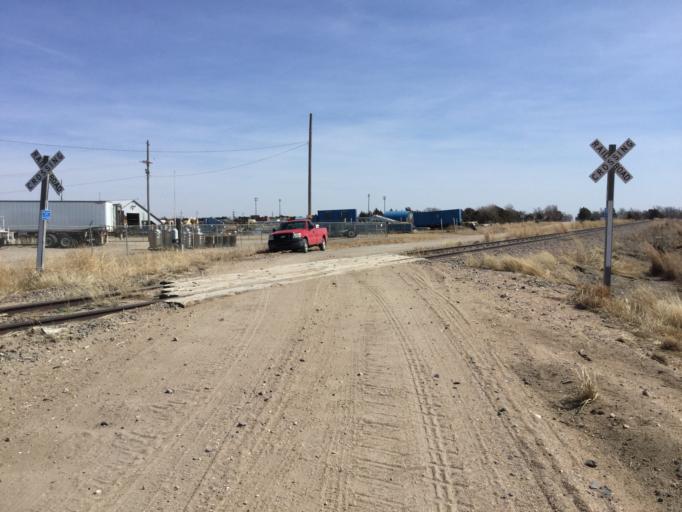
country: US
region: Kansas
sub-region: Rush County
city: La Crosse
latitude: 38.5368
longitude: -99.0640
